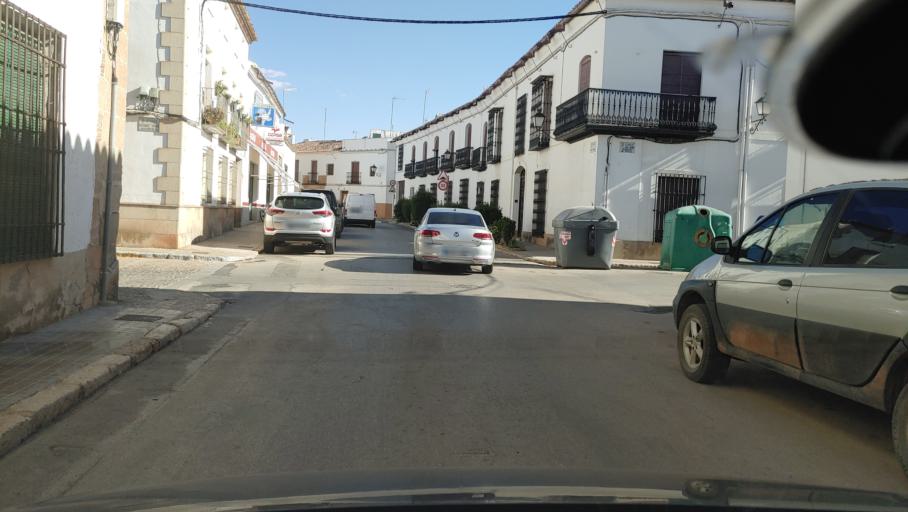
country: ES
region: Castille-La Mancha
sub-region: Provincia de Ciudad Real
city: Infantes
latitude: 38.7367
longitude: -3.0162
